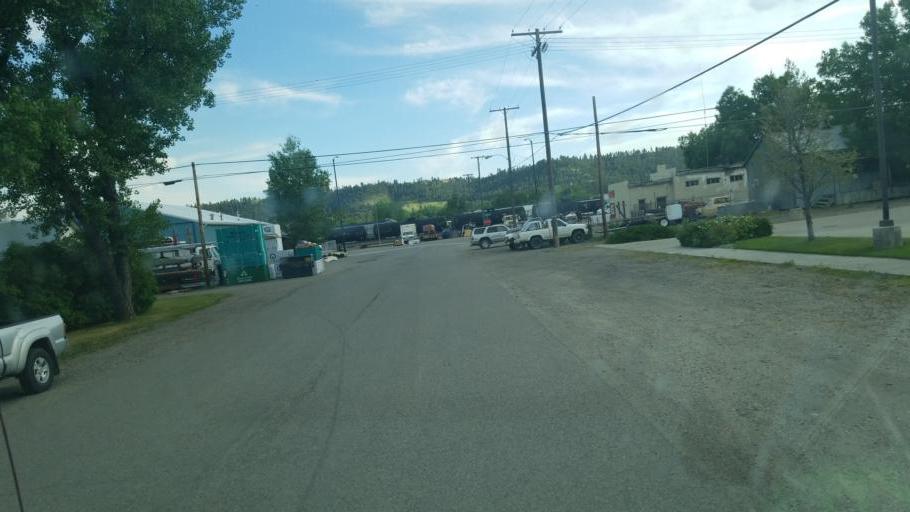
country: US
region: Montana
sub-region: Stillwater County
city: Columbus
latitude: 45.6374
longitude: -109.2507
